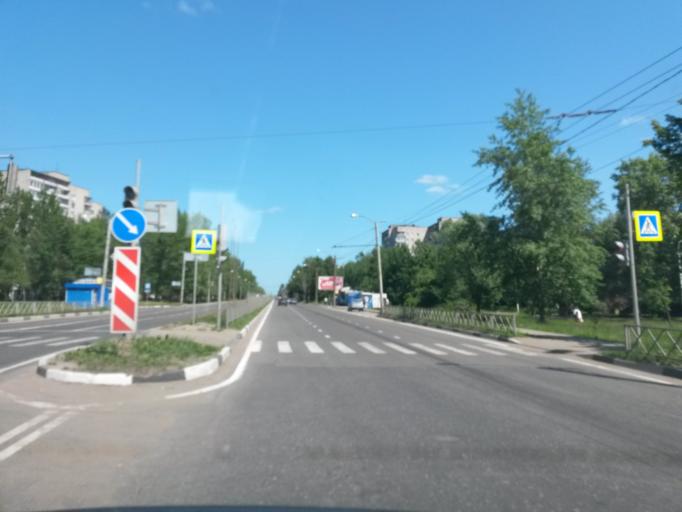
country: RU
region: Jaroslavl
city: Yaroslavl
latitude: 57.6747
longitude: 39.7736
